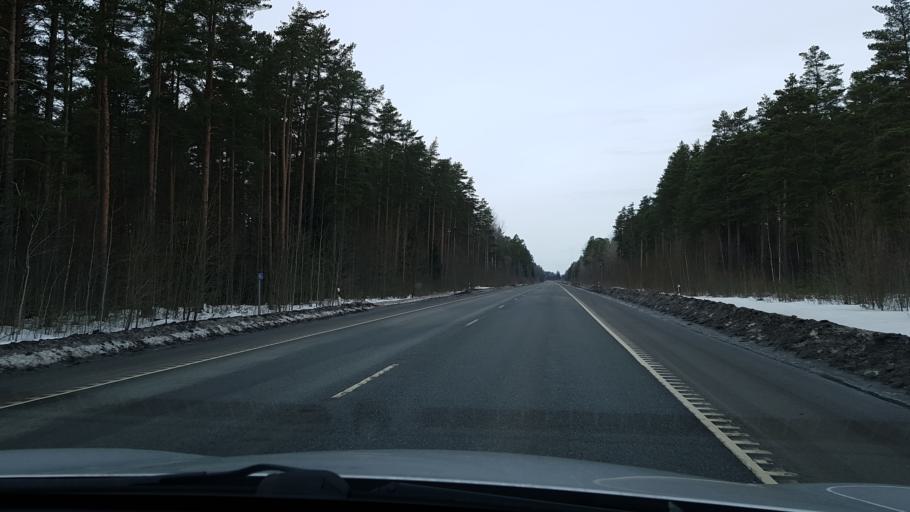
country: EE
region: Tartu
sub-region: Tartu linn
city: Tartu
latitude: 58.3947
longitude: 26.6625
